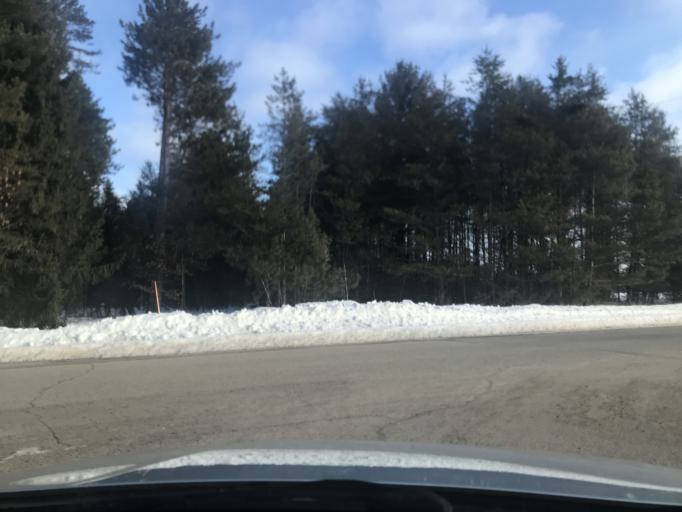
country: US
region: Wisconsin
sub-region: Marinette County
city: Niagara
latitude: 45.6261
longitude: -87.9768
